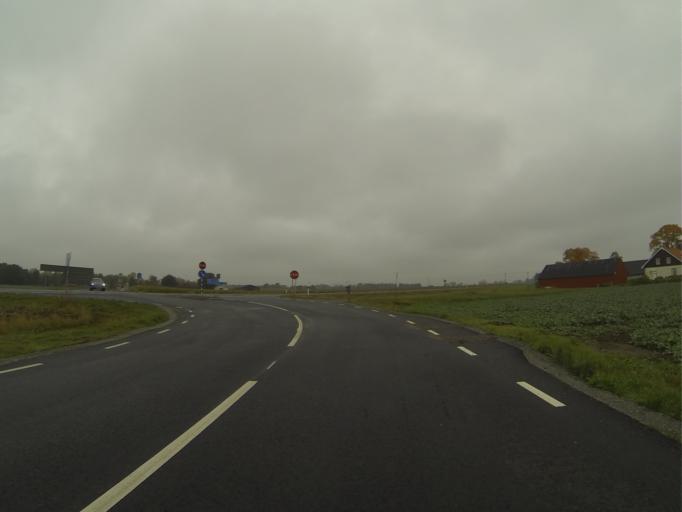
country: SE
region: Skane
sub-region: Tomelilla Kommun
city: Tomelilla
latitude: 55.5726
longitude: 13.9289
